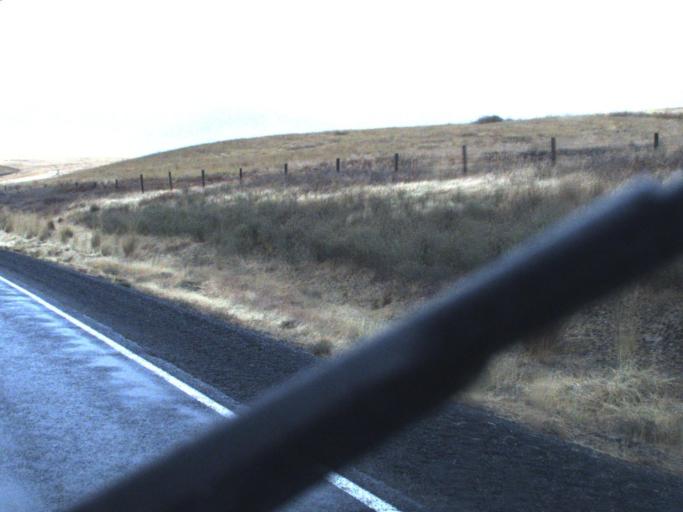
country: US
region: Washington
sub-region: Spokane County
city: Cheney
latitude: 47.1172
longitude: -117.6692
